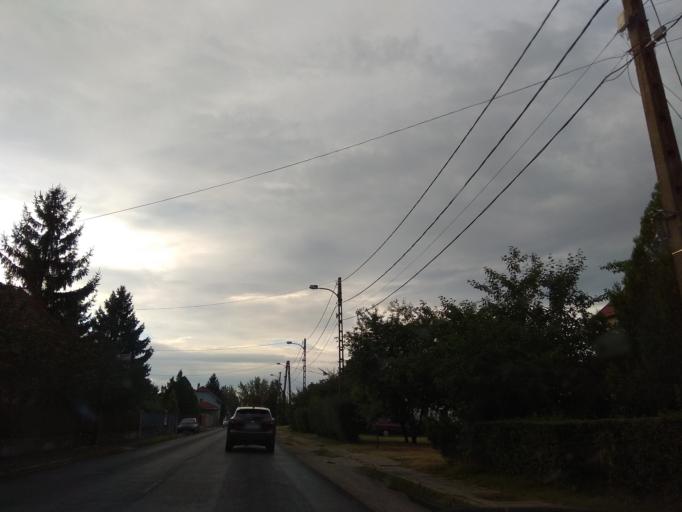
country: HU
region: Borsod-Abauj-Zemplen
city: Miskolc
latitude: 48.0929
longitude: 20.8063
